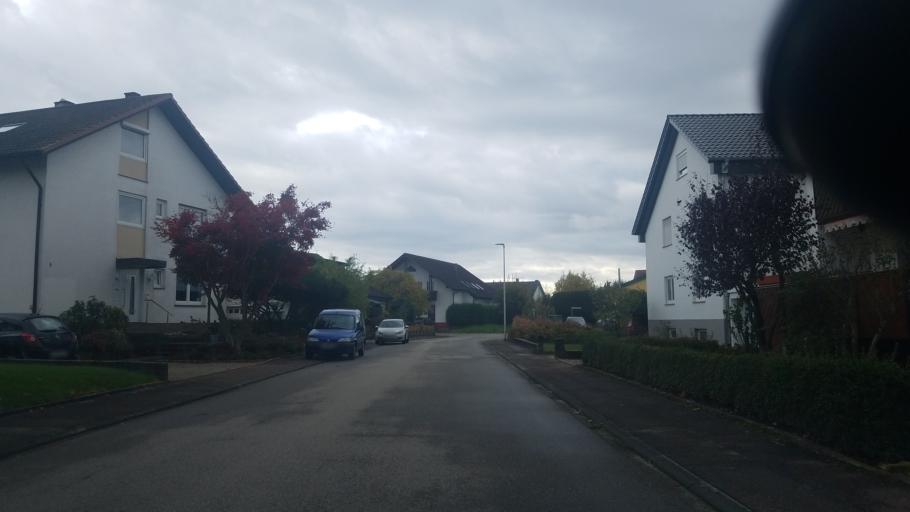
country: DE
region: Baden-Wuerttemberg
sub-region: Karlsruhe Region
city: Zell
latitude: 48.6565
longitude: 8.0248
